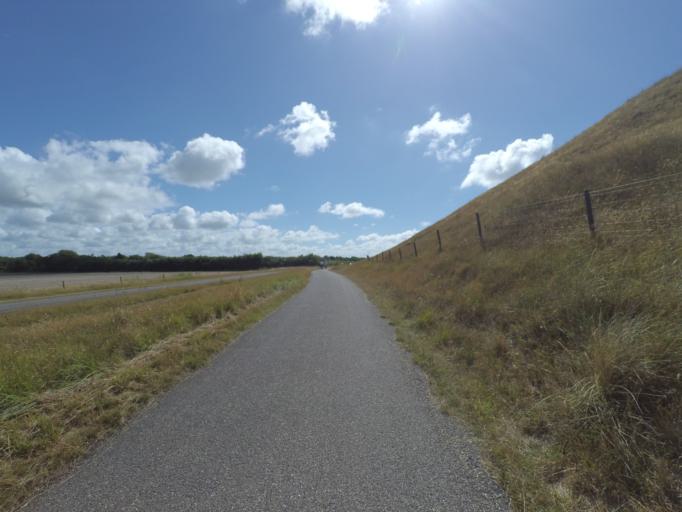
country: NL
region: North Holland
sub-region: Gemeente Texel
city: Den Burg
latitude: 53.1297
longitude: 4.8152
